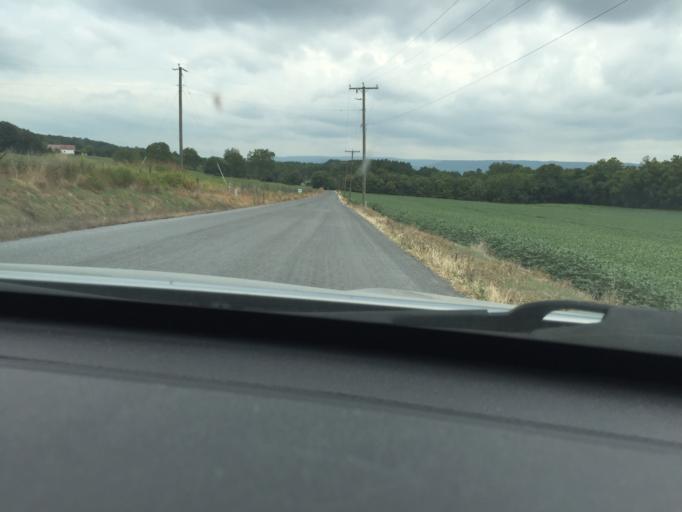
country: US
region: Virginia
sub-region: Shenandoah County
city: Woodstock
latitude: 38.8772
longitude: -78.4702
